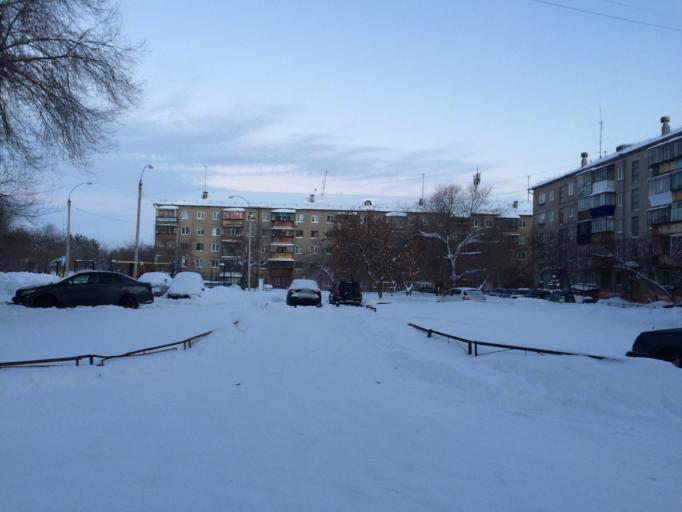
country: RU
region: Chelyabinsk
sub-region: Gorod Magnitogorsk
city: Magnitogorsk
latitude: 53.4052
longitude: 58.9729
